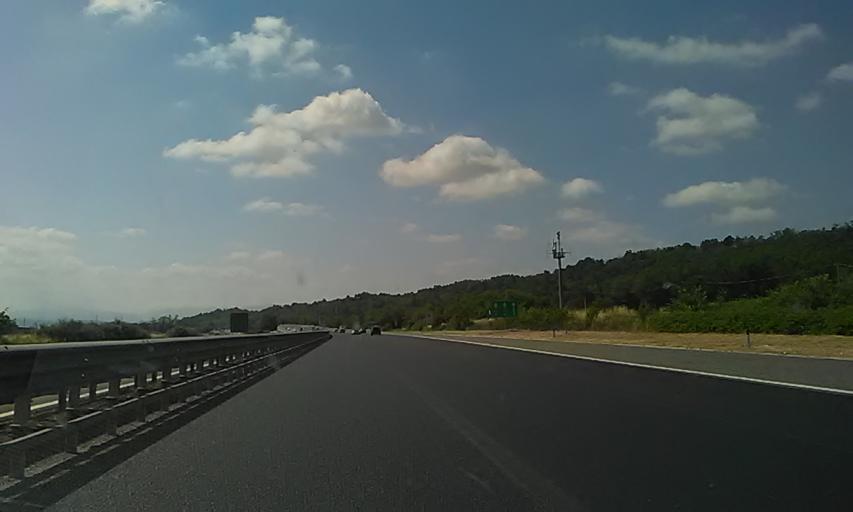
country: IT
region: Piedmont
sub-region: Provincia di Alessandria
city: Predosa
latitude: 44.7525
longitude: 8.6463
